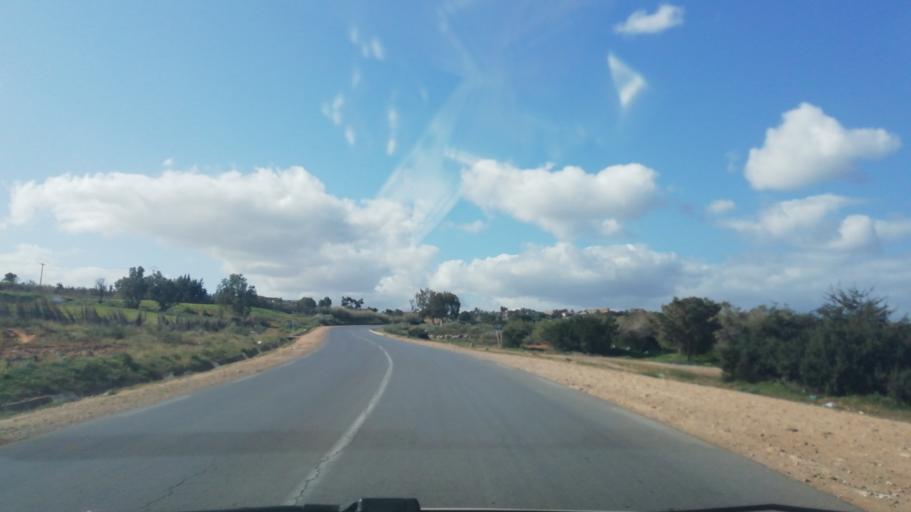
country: DZ
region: Relizane
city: Mazouna
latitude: 36.2913
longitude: 0.6524
